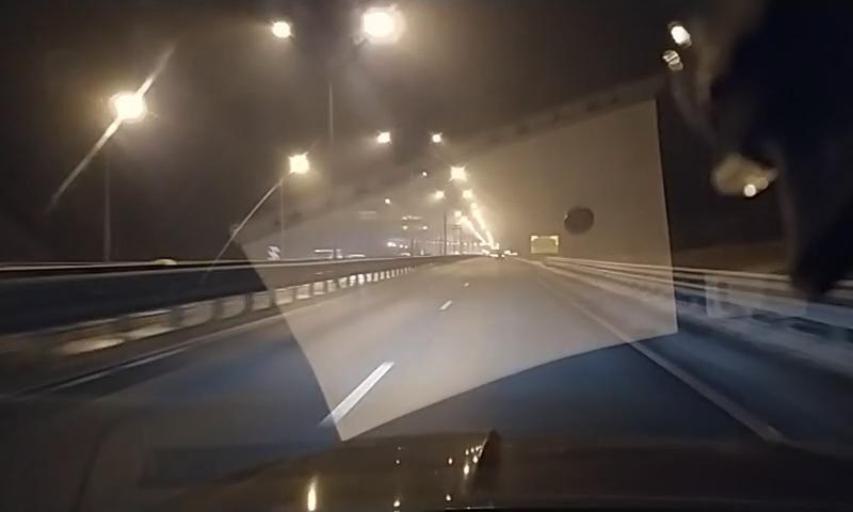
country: RU
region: Leningrad
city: Bugry
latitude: 60.1018
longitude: 30.3848
